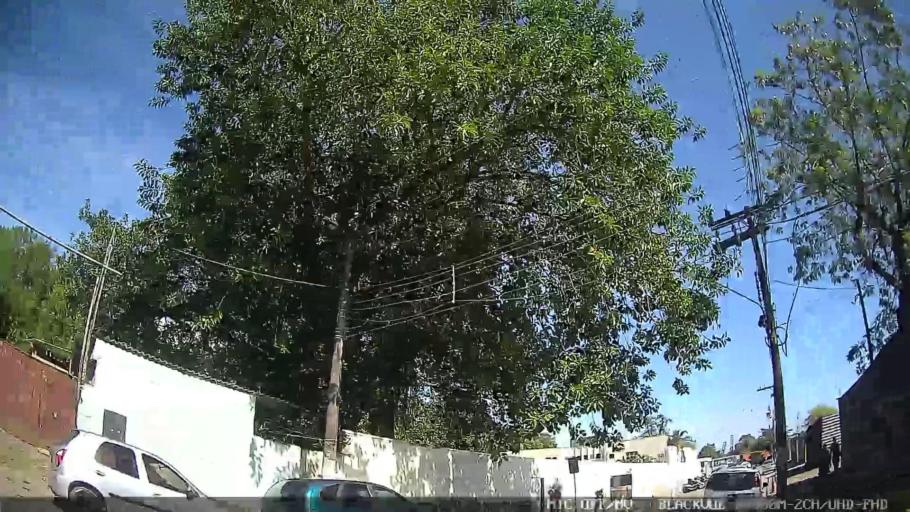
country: BR
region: Sao Paulo
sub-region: Guaruja
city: Guaruja
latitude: -23.9683
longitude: -46.2783
